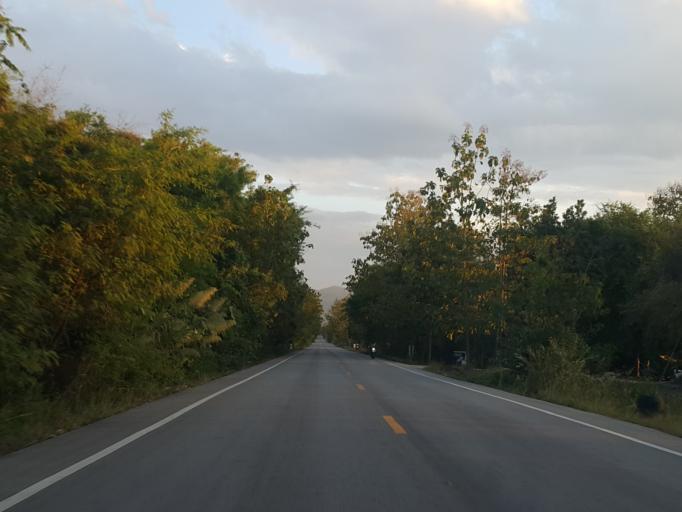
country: TH
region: Lampang
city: Mae Mo
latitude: 18.4425
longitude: 99.6378
